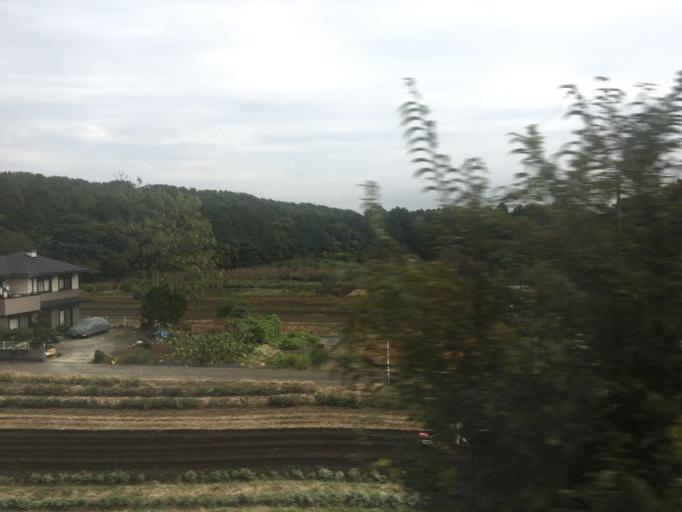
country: JP
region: Tokyo
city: Fussa
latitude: 35.7935
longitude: 139.3373
